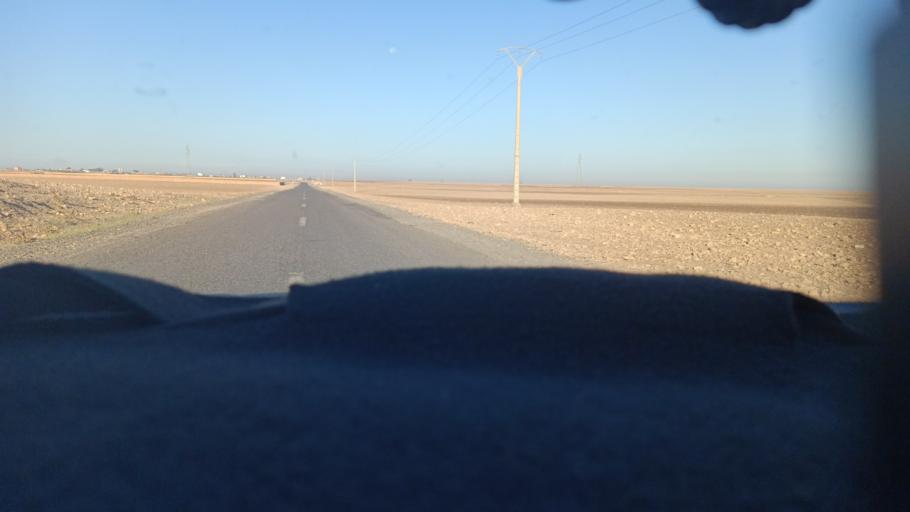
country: MA
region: Doukkala-Abda
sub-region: Safi
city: Youssoufia
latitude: 32.3708
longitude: -8.6557
